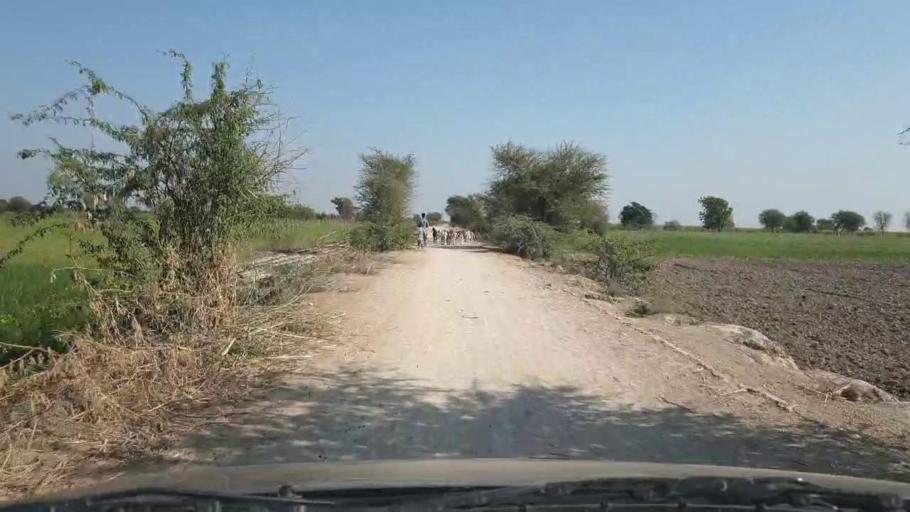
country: PK
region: Sindh
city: Samaro
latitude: 25.1983
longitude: 69.2698
